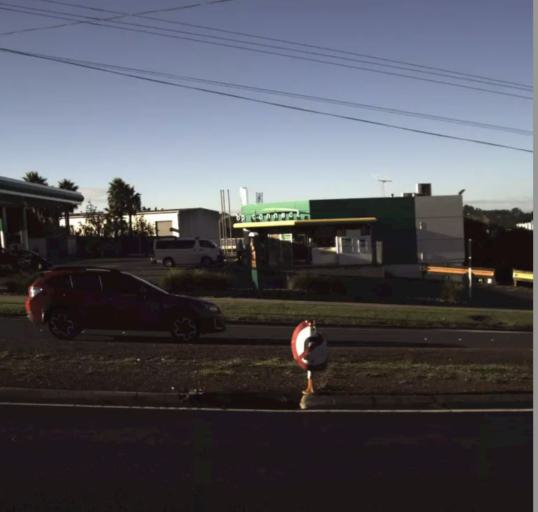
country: NZ
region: Auckland
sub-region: Auckland
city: Rothesay Bay
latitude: -36.6164
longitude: 174.6799
